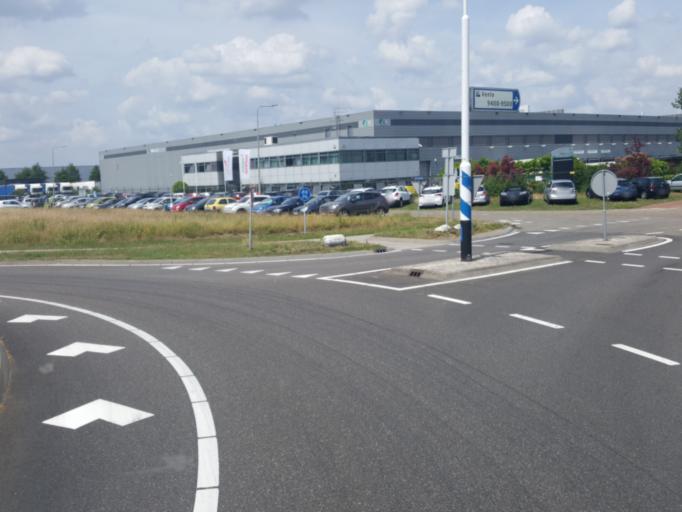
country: NL
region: Limburg
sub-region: Gemeente Peel en Maas
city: Maasbree
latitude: 51.3991
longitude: 6.0784
